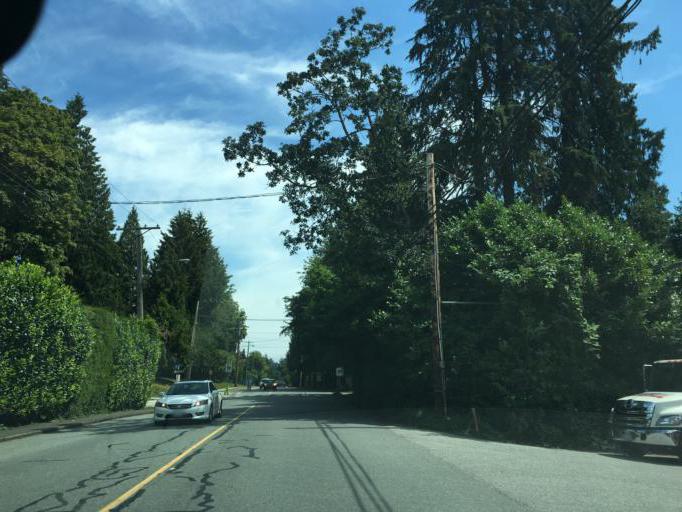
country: CA
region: British Columbia
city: West Vancouver
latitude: 49.3408
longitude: -123.2398
